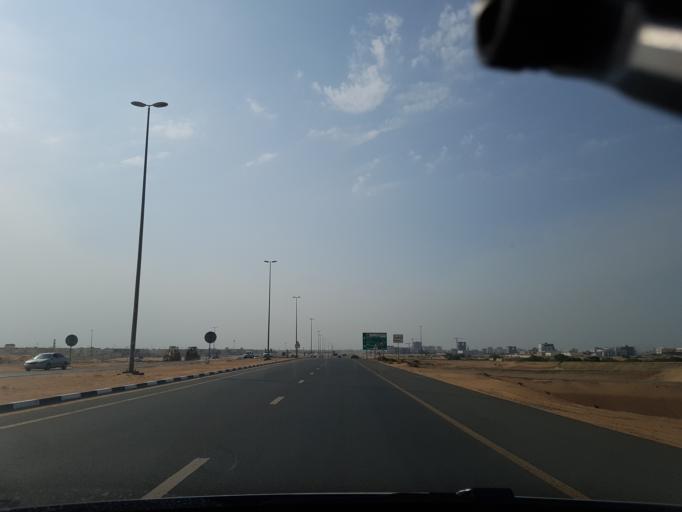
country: AE
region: Ajman
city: Ajman
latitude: 25.4132
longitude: 55.5589
